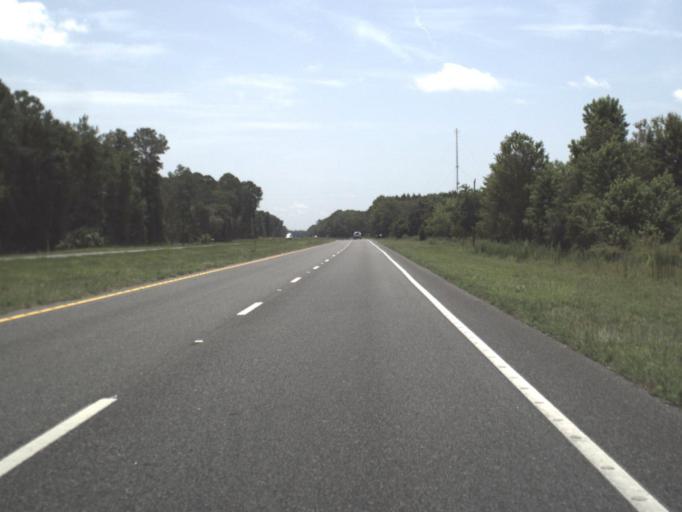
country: US
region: Florida
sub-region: Taylor County
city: Perry
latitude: 29.9662
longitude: -83.4752
